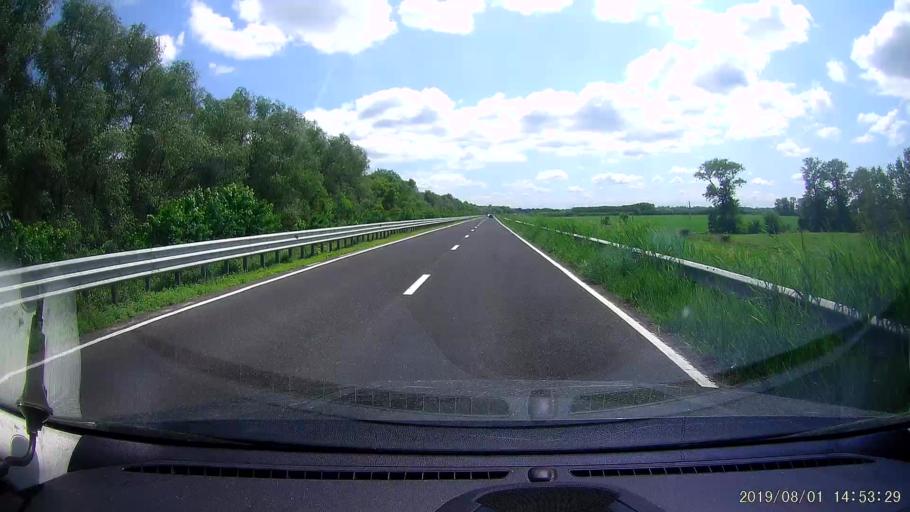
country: RO
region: Braila
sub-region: Municipiul Braila
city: Braila
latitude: 45.3341
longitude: 28.0024
